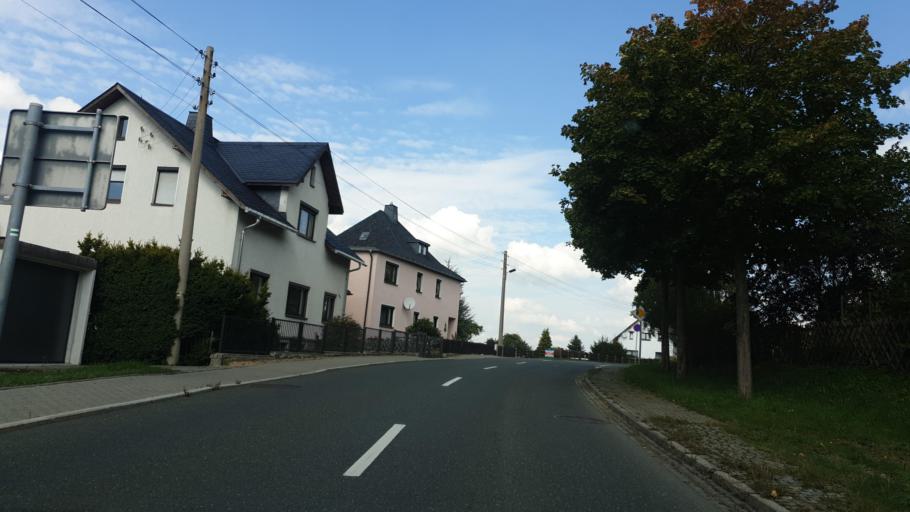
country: DE
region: Saxony
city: Rodewisch
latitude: 50.5079
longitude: 12.4622
